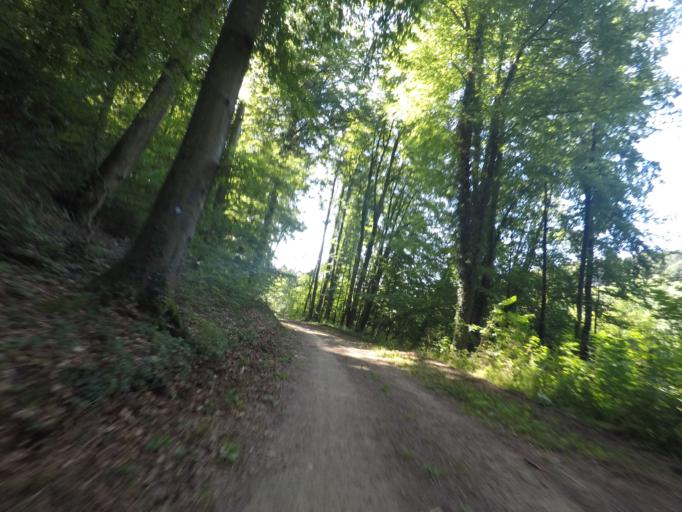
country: LU
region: Luxembourg
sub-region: Canton de Capellen
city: Kopstal
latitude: 49.6510
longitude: 6.0601
